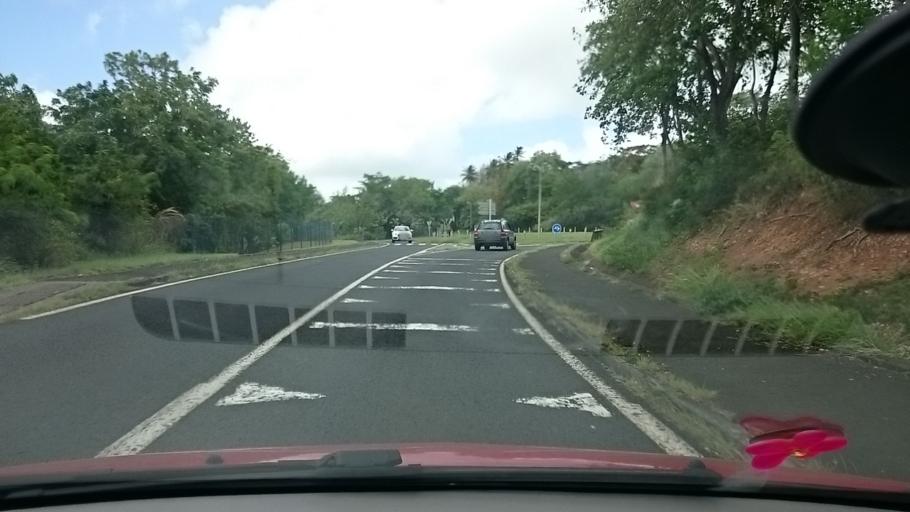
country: MQ
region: Martinique
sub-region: Martinique
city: La Trinite
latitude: 14.7431
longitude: -60.9471
